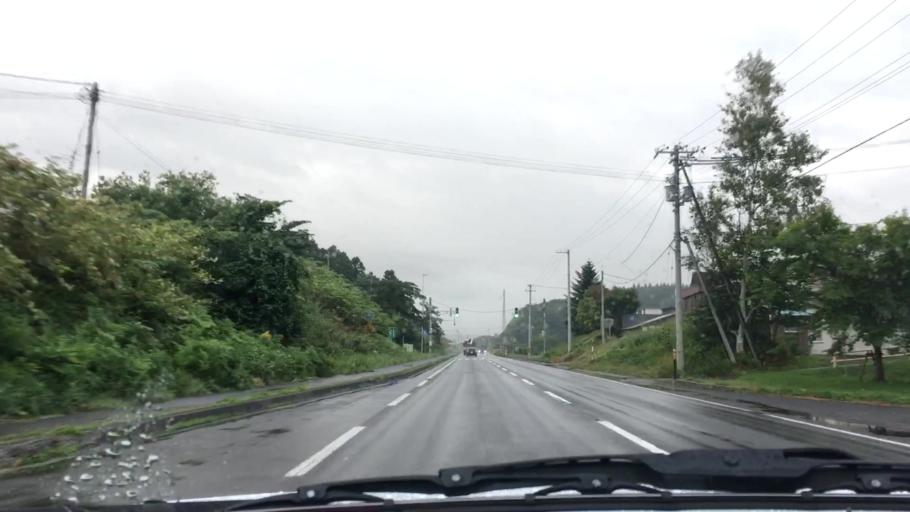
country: JP
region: Hokkaido
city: Nanae
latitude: 42.1748
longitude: 140.4535
